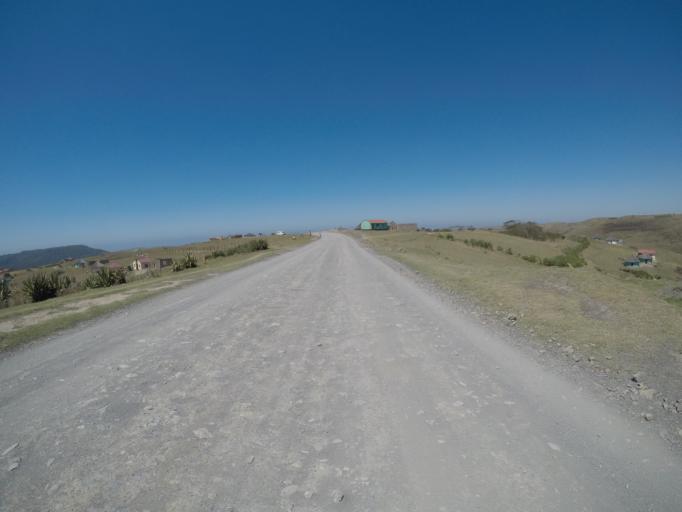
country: ZA
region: Eastern Cape
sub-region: OR Tambo District Municipality
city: Libode
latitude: -31.9935
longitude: 29.0543
